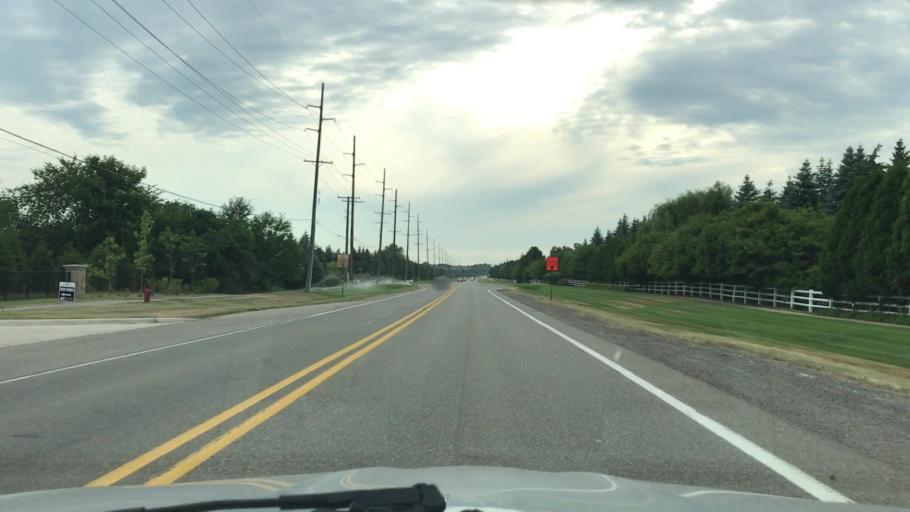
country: US
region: Michigan
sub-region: Wayne County
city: Northville
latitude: 42.4079
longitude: -83.5204
